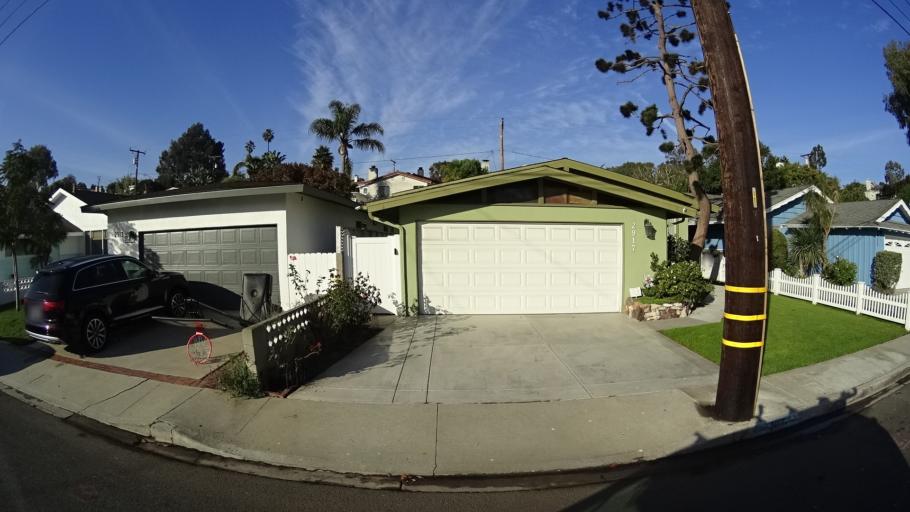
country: US
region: California
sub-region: Los Angeles County
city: Manhattan Beach
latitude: 33.8976
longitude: -118.4035
